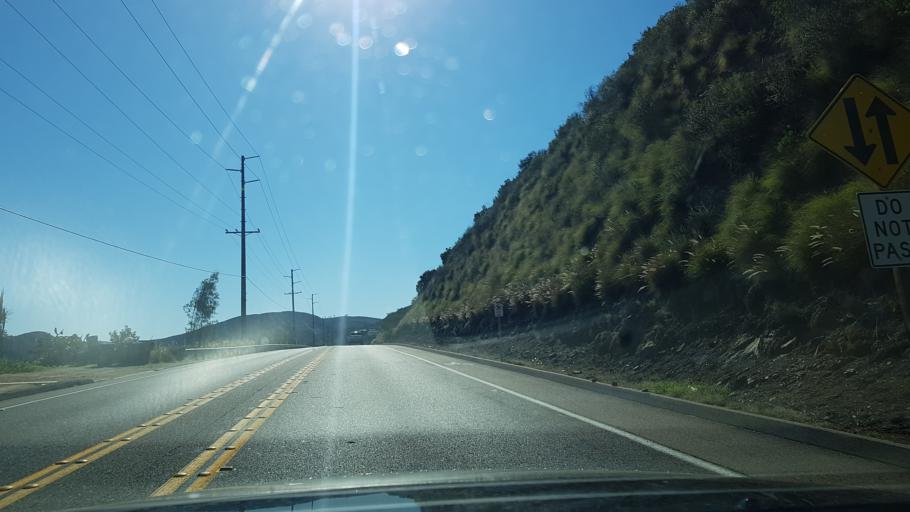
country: US
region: California
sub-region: San Diego County
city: Escondido
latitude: 33.0728
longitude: -117.1216
